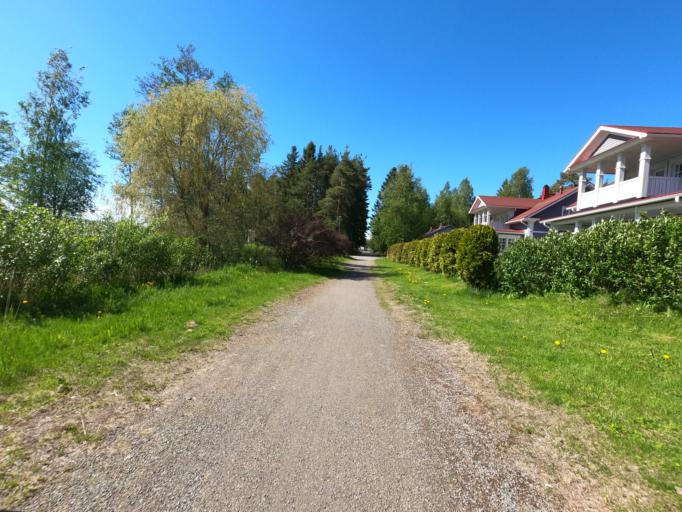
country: FI
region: North Karelia
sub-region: Joensuu
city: Joensuu
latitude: 62.5799
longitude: 29.7678
